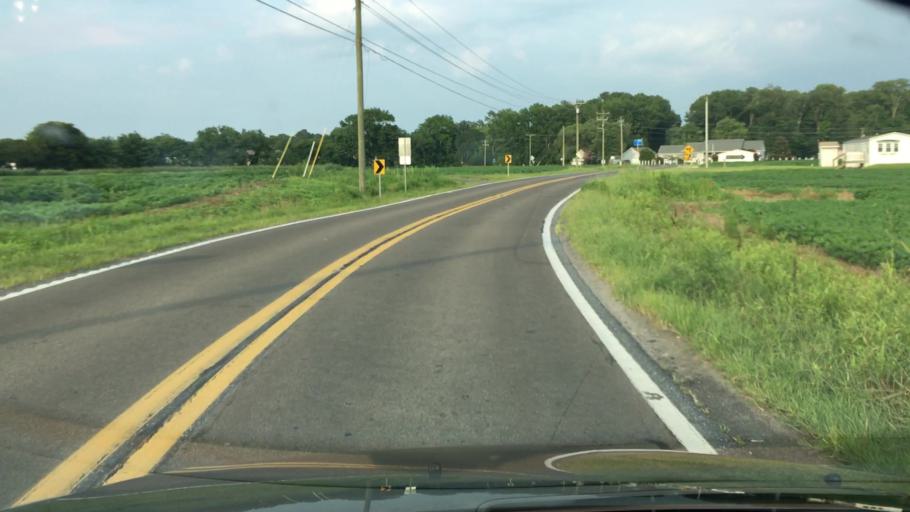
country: US
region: Delaware
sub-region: Sussex County
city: Ocean View
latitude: 38.5048
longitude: -75.1256
